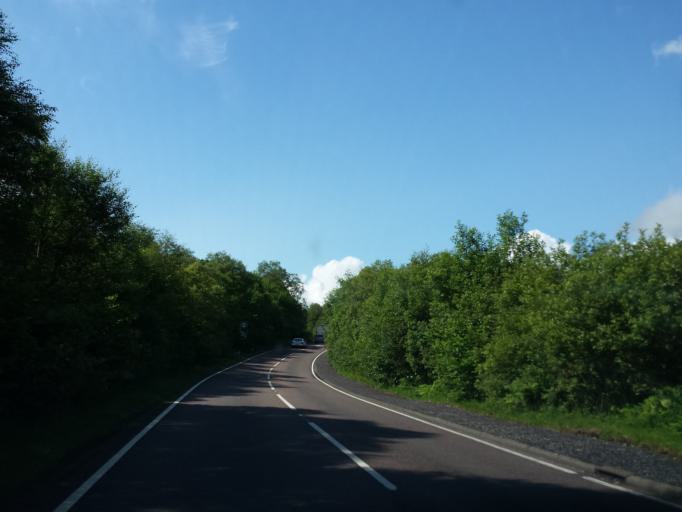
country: GB
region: Scotland
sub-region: Argyll and Bute
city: Garelochhead
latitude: 56.4062
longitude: -5.0342
